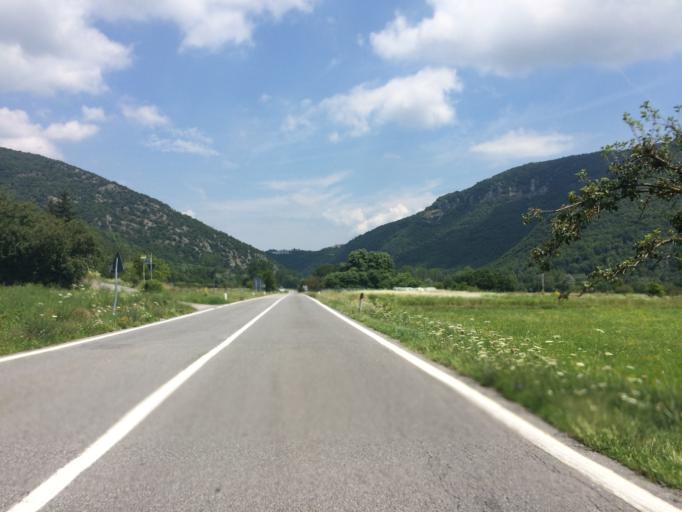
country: IT
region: Piedmont
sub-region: Provincia di Cuneo
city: Priola
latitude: 44.2642
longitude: 8.0264
